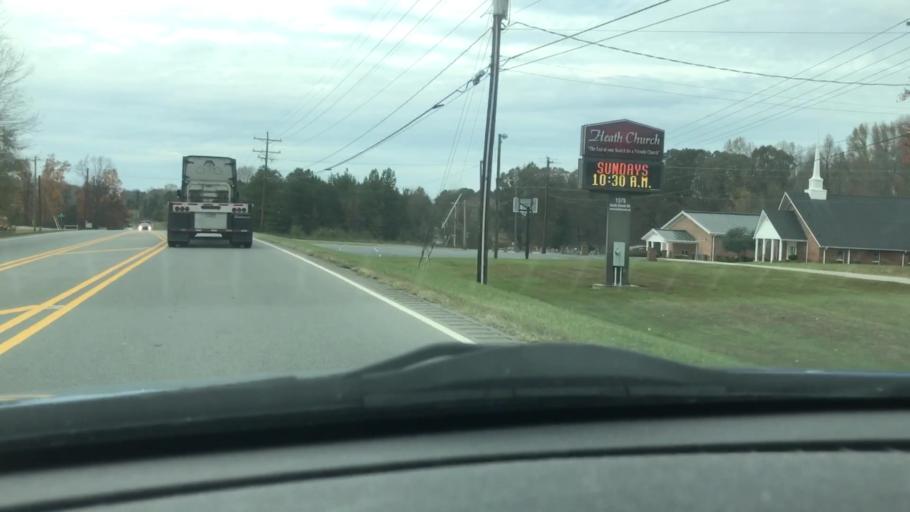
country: US
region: North Carolina
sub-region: Davidson County
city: Lexington
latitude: 35.8021
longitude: -80.1589
